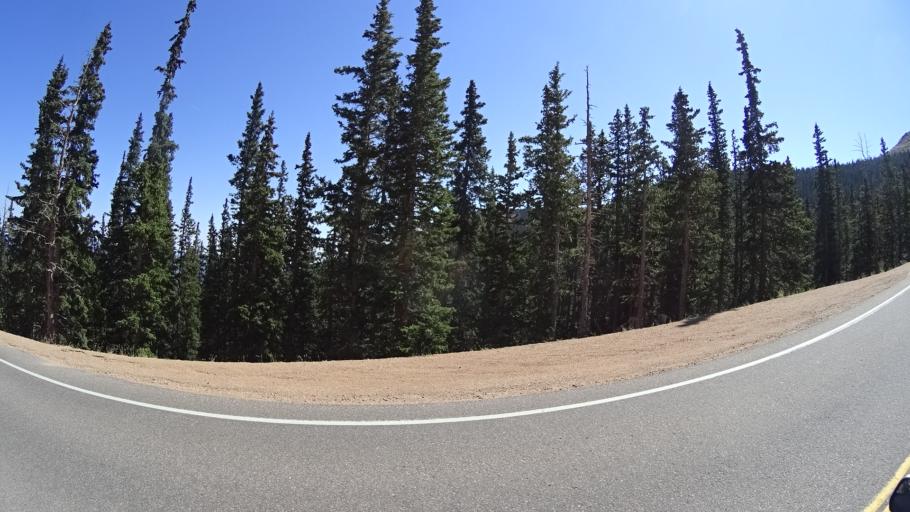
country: US
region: Colorado
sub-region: El Paso County
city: Cascade-Chipita Park
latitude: 38.8789
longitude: -105.0740
